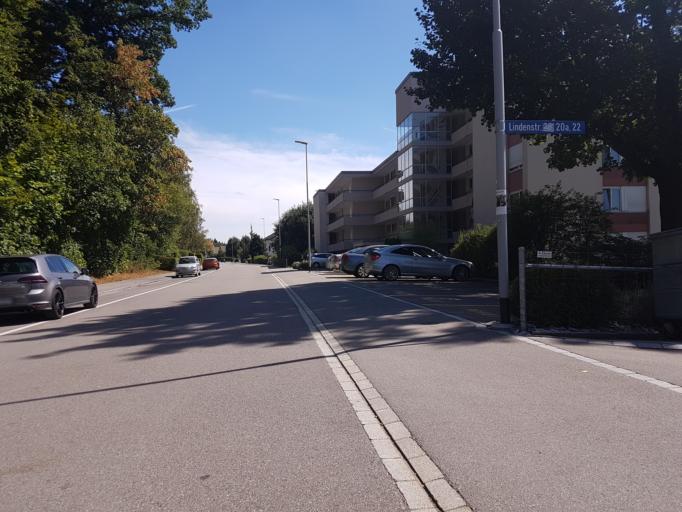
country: CH
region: Zurich
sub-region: Bezirk Pfaeffikon
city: Effretikon / Watt
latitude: 47.4276
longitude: 8.6980
